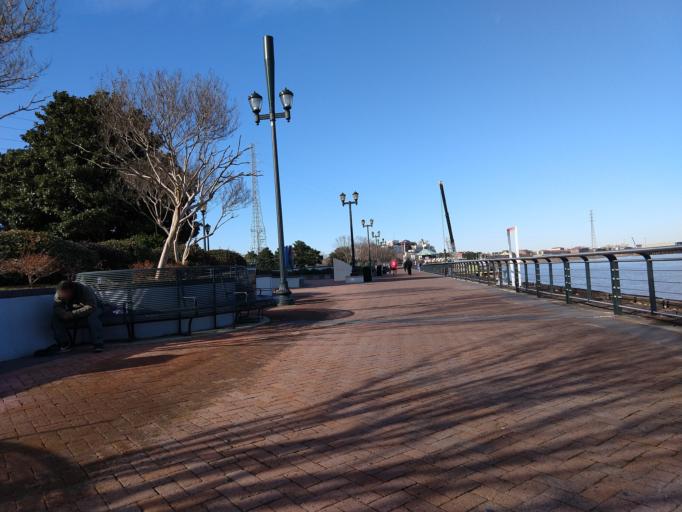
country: US
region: Louisiana
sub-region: Orleans Parish
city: New Orleans
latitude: 29.9519
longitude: -90.0627
